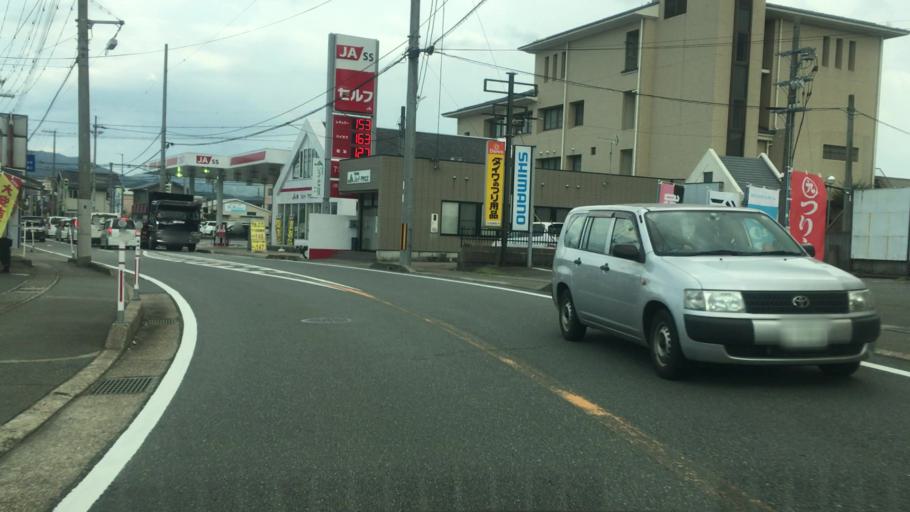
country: JP
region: Hyogo
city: Toyooka
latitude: 35.5348
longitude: 134.8187
